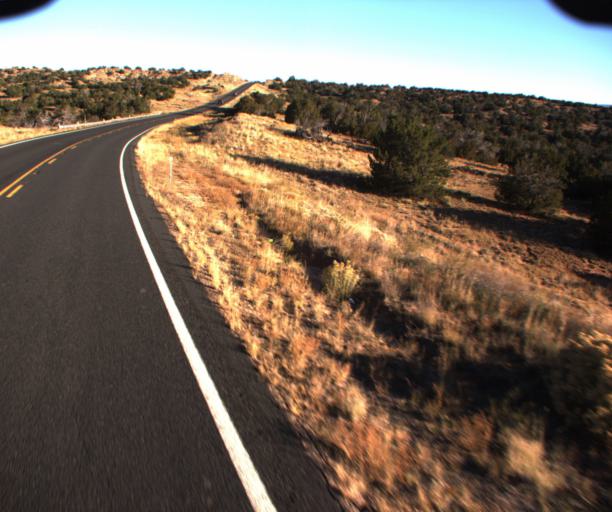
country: US
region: Arizona
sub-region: Apache County
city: Ganado
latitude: 35.4355
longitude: -109.5228
